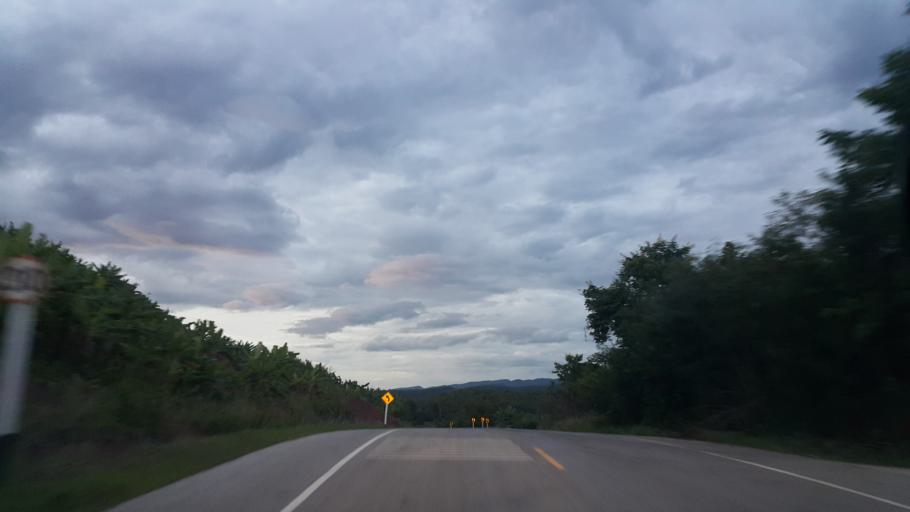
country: TH
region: Loei
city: Phu Ruea
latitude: 17.5222
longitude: 101.2328
